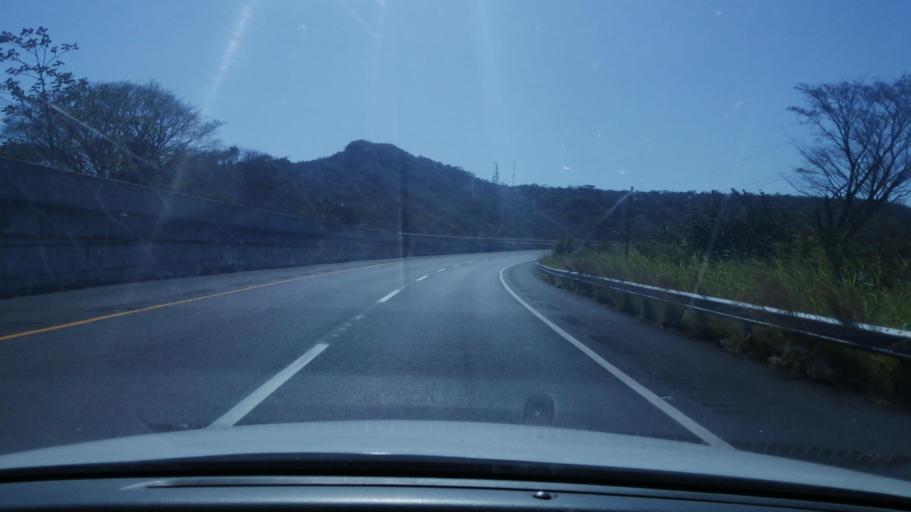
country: PA
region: Chiriqui
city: San Felix
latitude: 8.2785
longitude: -82.0534
